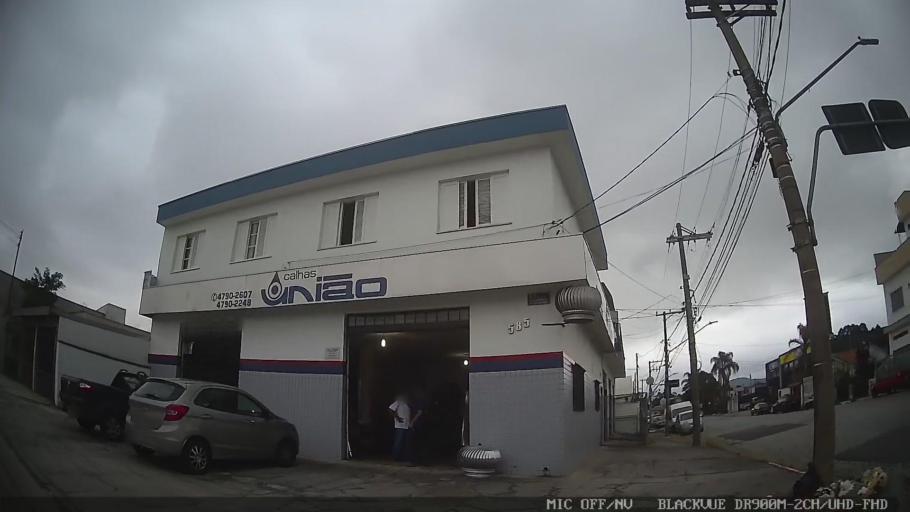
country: BR
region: Sao Paulo
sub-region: Mogi das Cruzes
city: Mogi das Cruzes
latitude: -23.5160
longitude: -46.1963
